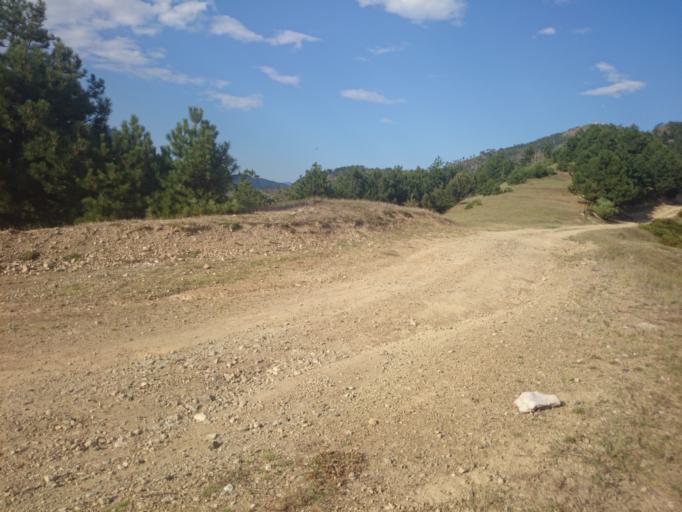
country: AL
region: Lezhe
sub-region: Rrethi i Mirdites
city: Orosh
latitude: 41.8645
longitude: 20.0741
